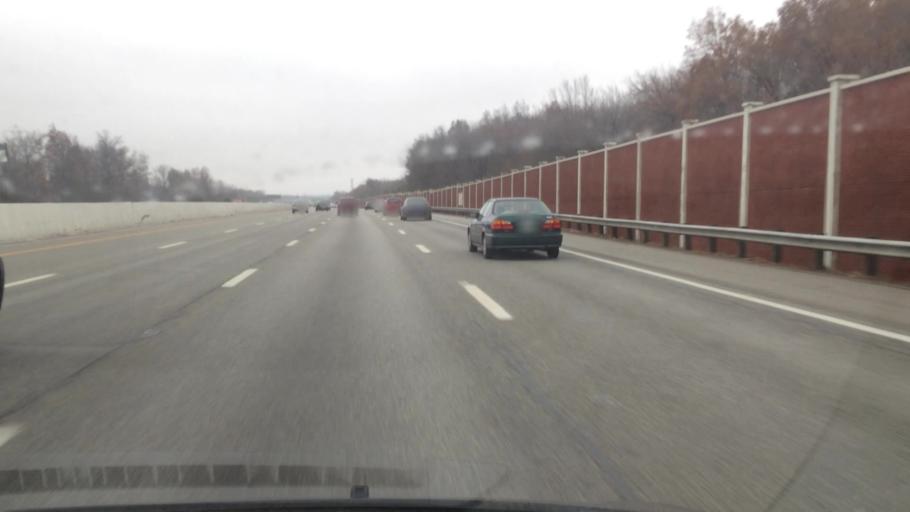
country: US
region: Ohio
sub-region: Cuyahoga County
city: Independence
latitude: 41.3757
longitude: -81.6527
